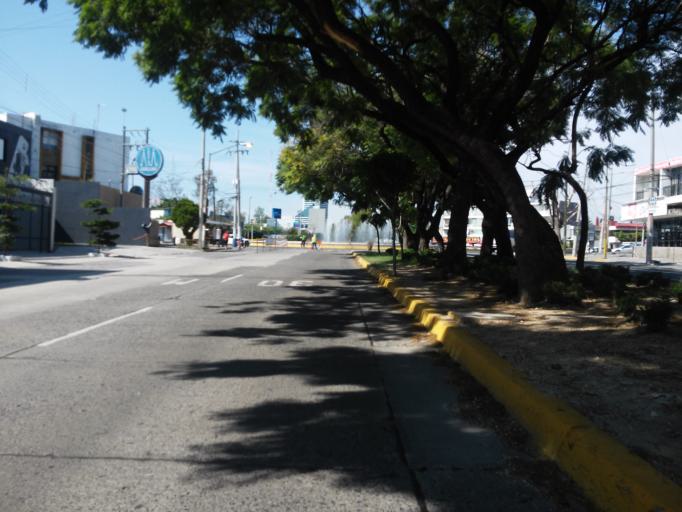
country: MX
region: Jalisco
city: Guadalajara
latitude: 20.6667
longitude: -103.3833
